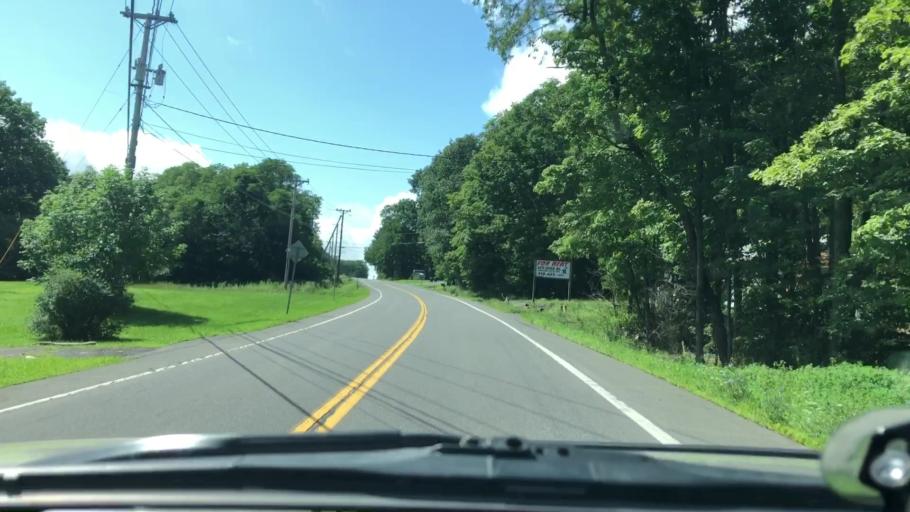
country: US
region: New York
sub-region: Greene County
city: Cairo
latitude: 42.2546
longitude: -73.9783
